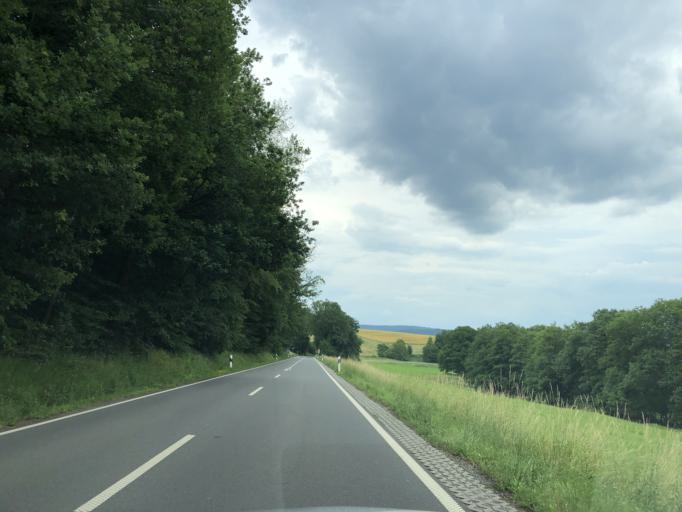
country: DE
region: Hesse
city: Michelstadt
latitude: 49.6972
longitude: 8.9758
